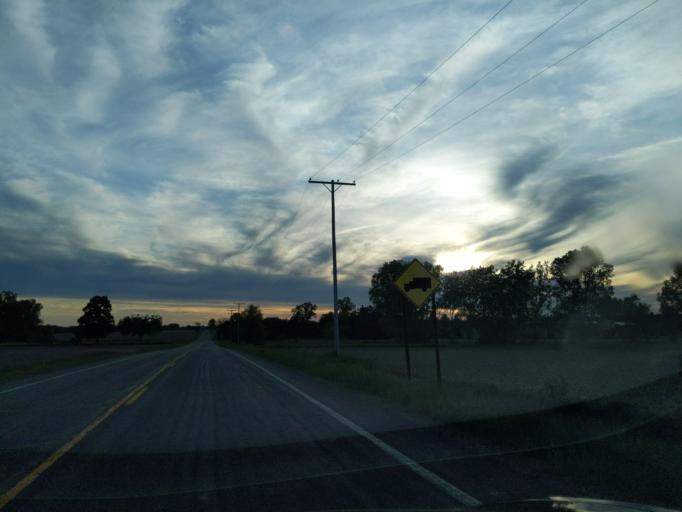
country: US
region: Michigan
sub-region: Ingham County
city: Williamston
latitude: 42.6010
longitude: -84.3028
